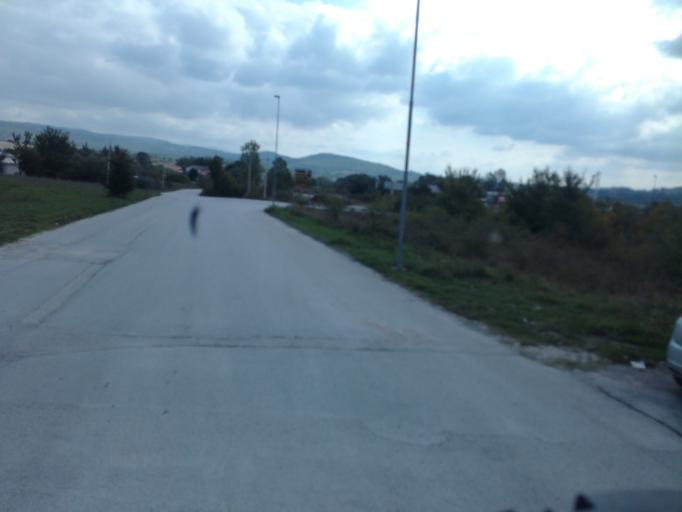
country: IT
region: Molise
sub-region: Provincia di Campobasso
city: Vinchiaturo
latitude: 41.4697
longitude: 14.5611
